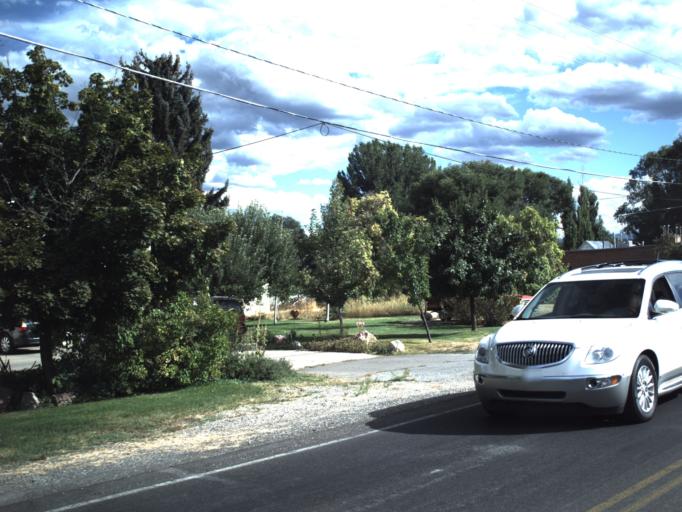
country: US
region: Utah
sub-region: Cache County
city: Hyrum
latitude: 41.6404
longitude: -111.8661
